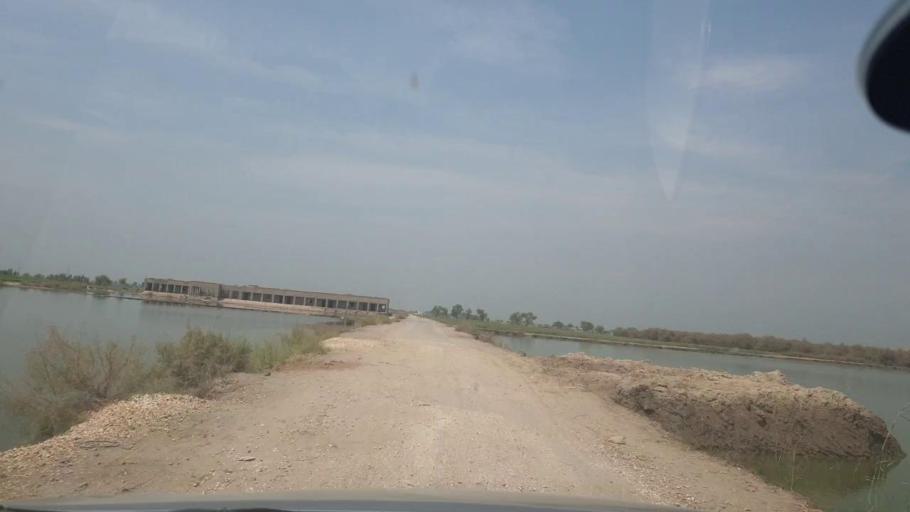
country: PK
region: Sindh
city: Thul
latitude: 28.1680
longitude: 68.6359
